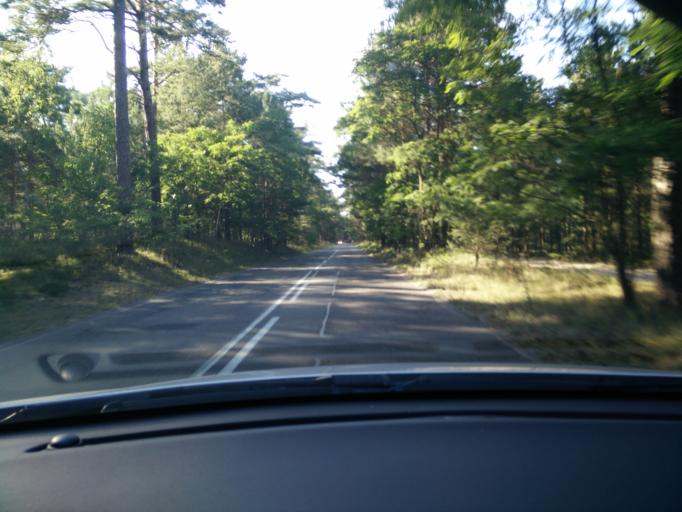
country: PL
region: Pomeranian Voivodeship
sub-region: Powiat pucki
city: Jastarnia
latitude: 54.6654
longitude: 18.7448
